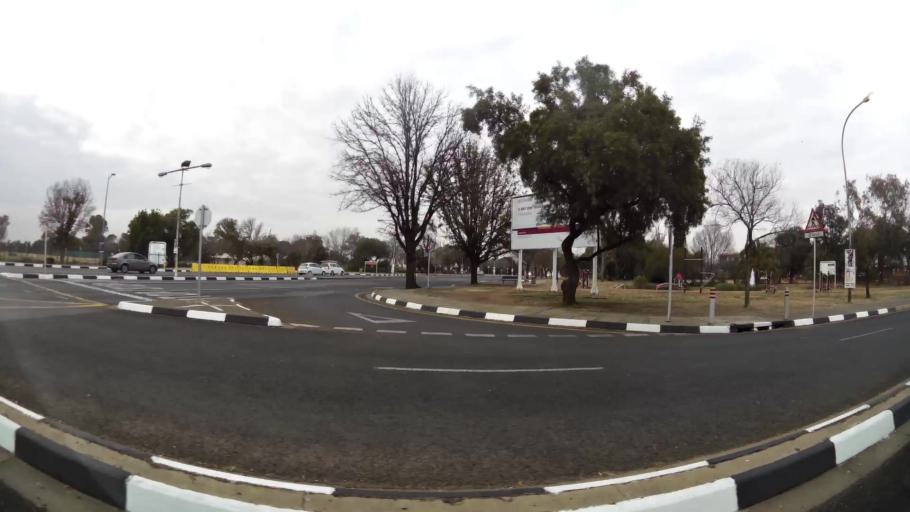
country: ZA
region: Orange Free State
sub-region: Mangaung Metropolitan Municipality
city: Bloemfontein
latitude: -29.1078
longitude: 26.1921
